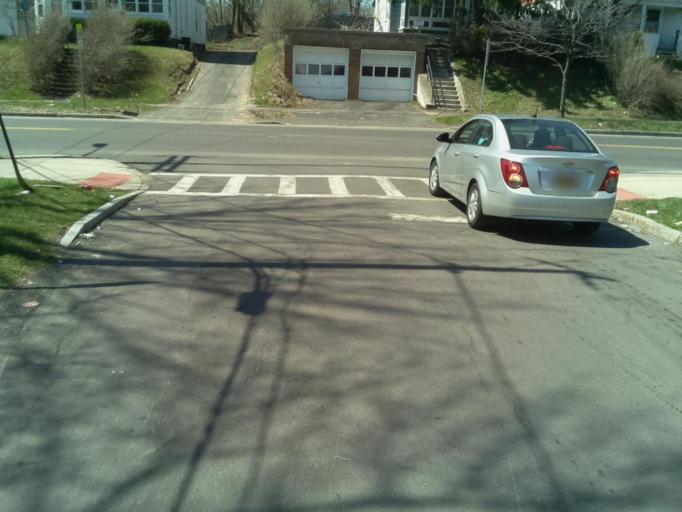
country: US
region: New York
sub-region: Onondaga County
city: Lyncourt
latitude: 43.0597
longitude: -76.1219
